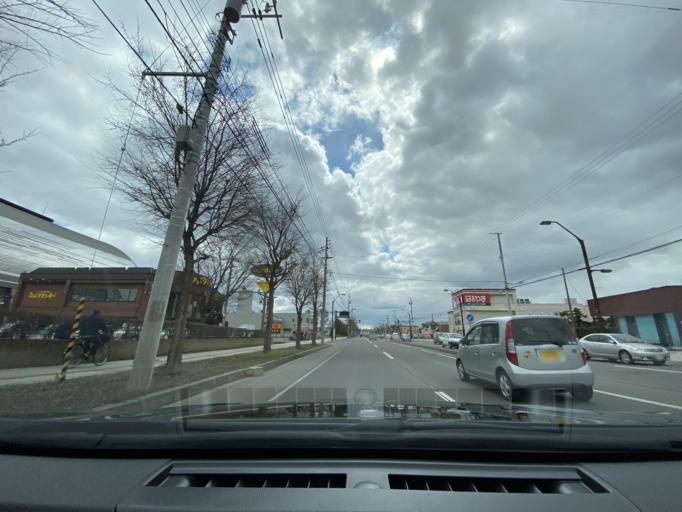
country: JP
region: Hokkaido
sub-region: Asahikawa-shi
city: Asahikawa
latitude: 43.7584
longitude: 142.3485
